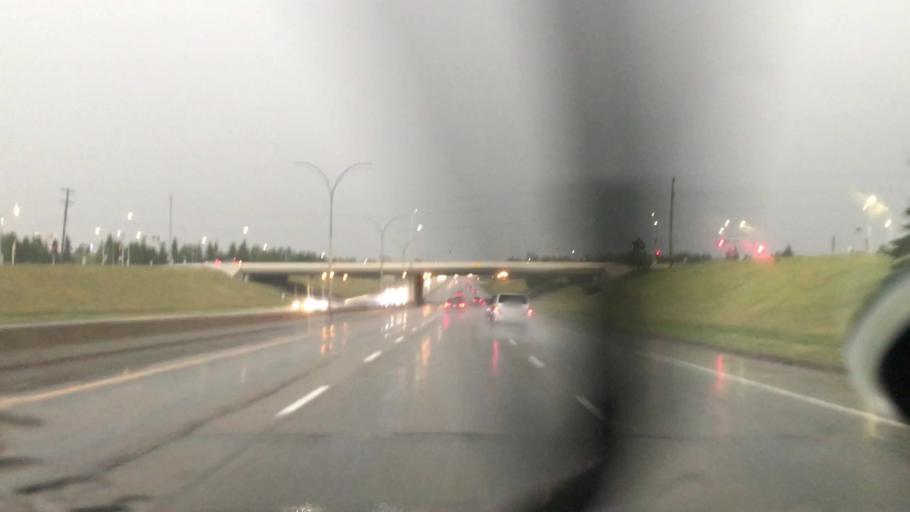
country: CA
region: Alberta
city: Edmonton
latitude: 53.4824
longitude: -113.4693
